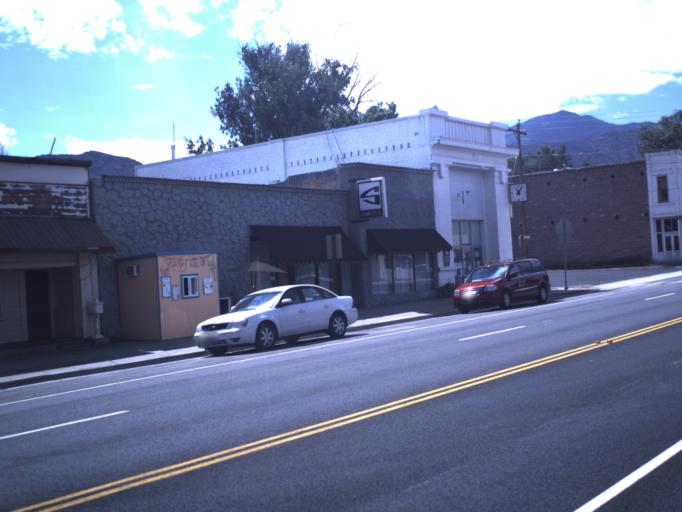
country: US
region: Utah
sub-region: Sevier County
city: Monroe
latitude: 38.6325
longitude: -112.1215
